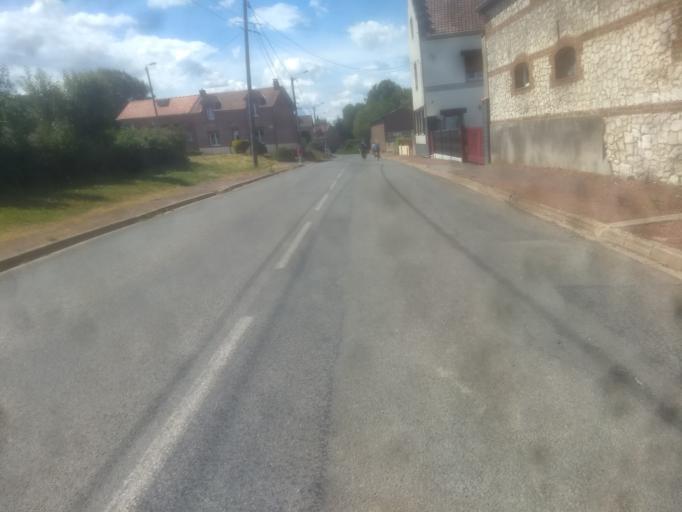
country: FR
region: Nord-Pas-de-Calais
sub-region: Departement du Pas-de-Calais
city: Tilloy-les-Mofflaines
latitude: 50.2484
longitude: 2.8264
